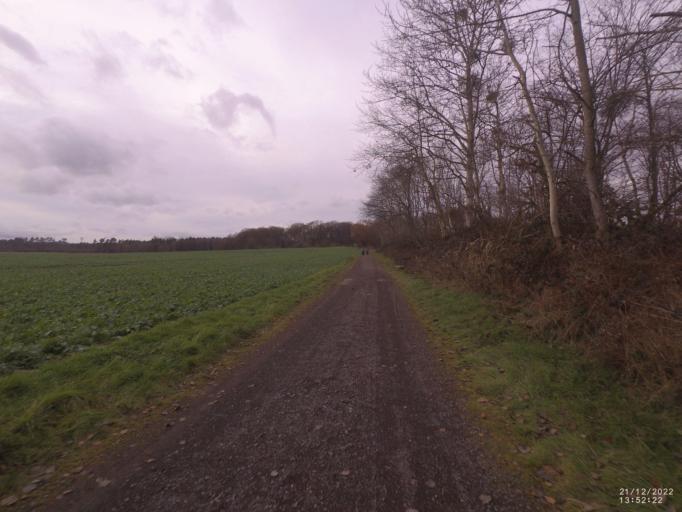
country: DE
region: Rheinland-Pfalz
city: Bad Breisig
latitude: 50.5133
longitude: 7.2613
